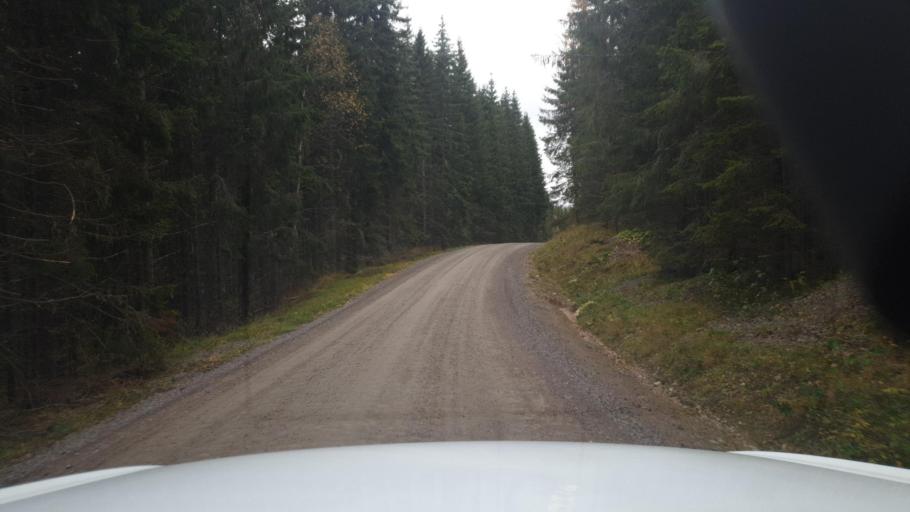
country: SE
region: Vaermland
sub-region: Arvika Kommun
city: Arvika
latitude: 59.9577
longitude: 12.6596
